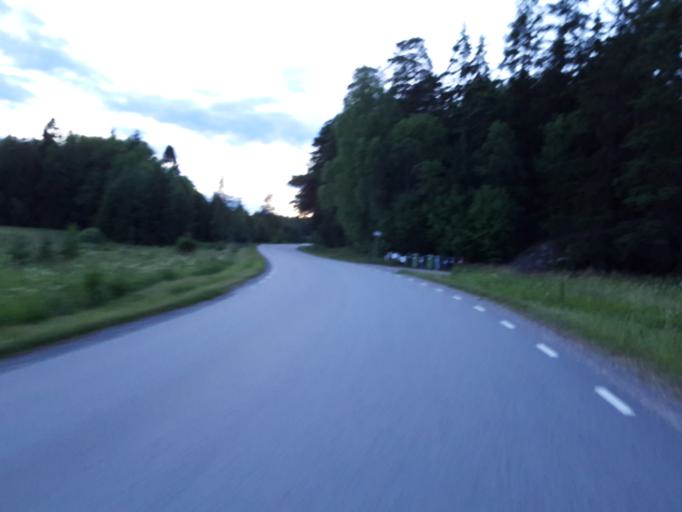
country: SE
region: Uppsala
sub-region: Uppsala Kommun
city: Uppsala
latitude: 59.7972
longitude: 17.5883
